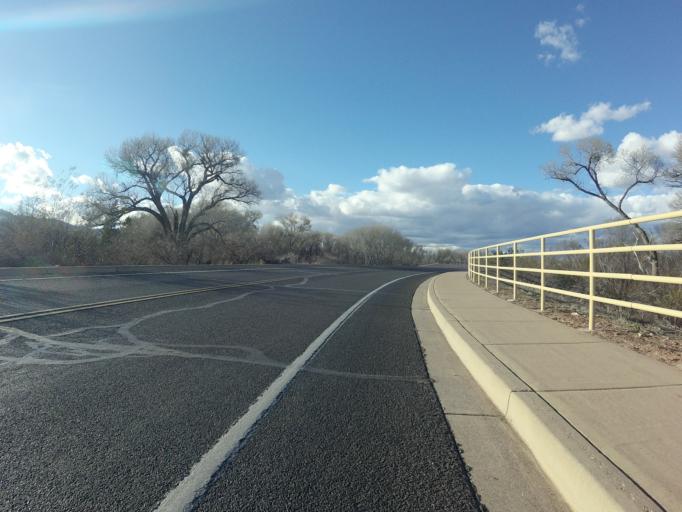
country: US
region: Arizona
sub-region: Yavapai County
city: Cottonwood
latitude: 34.7490
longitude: -112.0218
